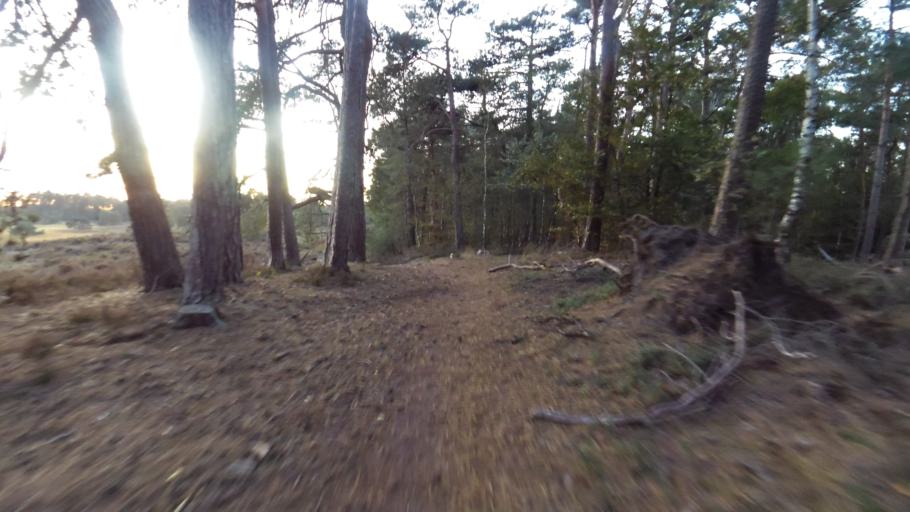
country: NL
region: Gelderland
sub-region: Gemeente Epe
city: Emst
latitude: 52.3443
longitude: 5.8938
